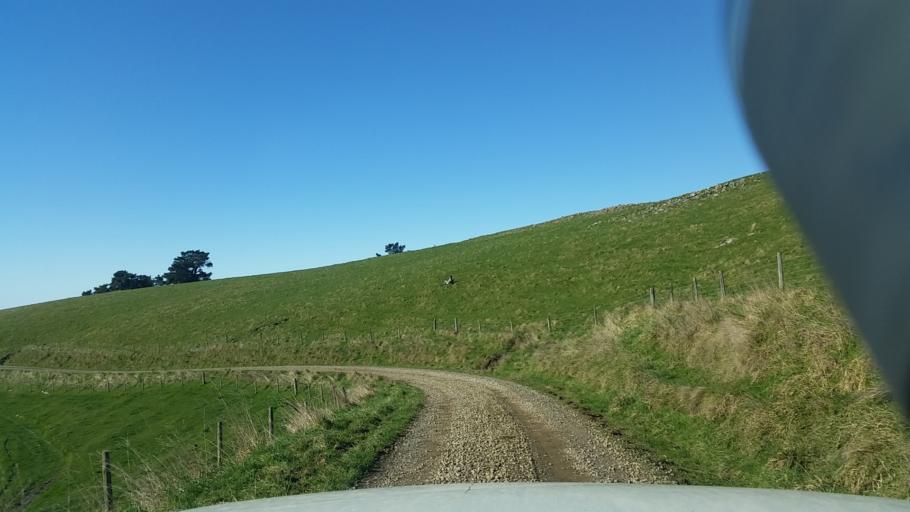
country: NZ
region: Canterbury
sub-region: Christchurch City
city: Christchurch
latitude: -43.6536
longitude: 172.9799
